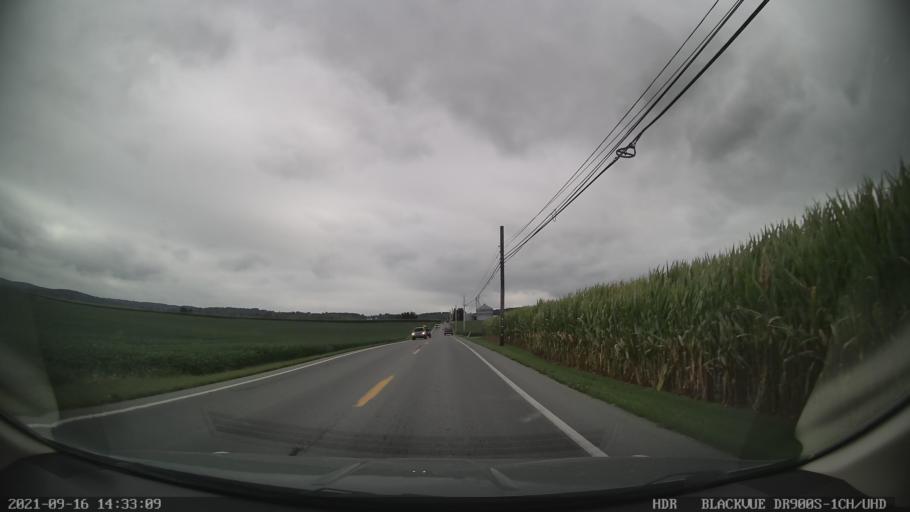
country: US
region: Pennsylvania
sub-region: Berks County
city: Kutztown
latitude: 40.4890
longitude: -75.7600
